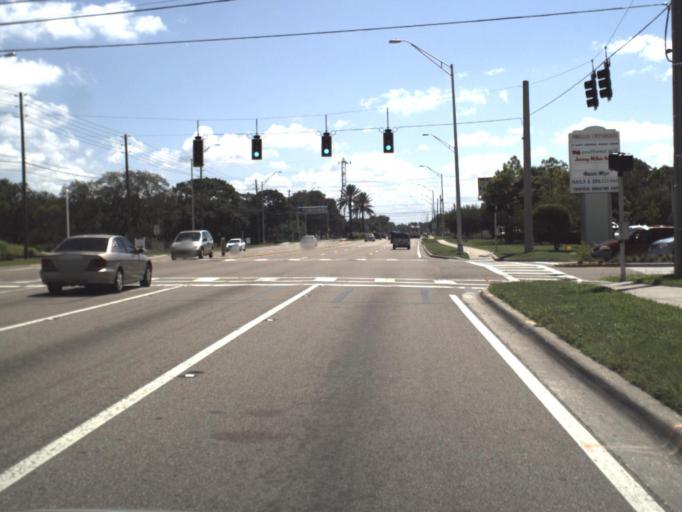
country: US
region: Florida
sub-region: Pinellas County
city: South Highpoint
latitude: 27.9162
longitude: -82.7265
